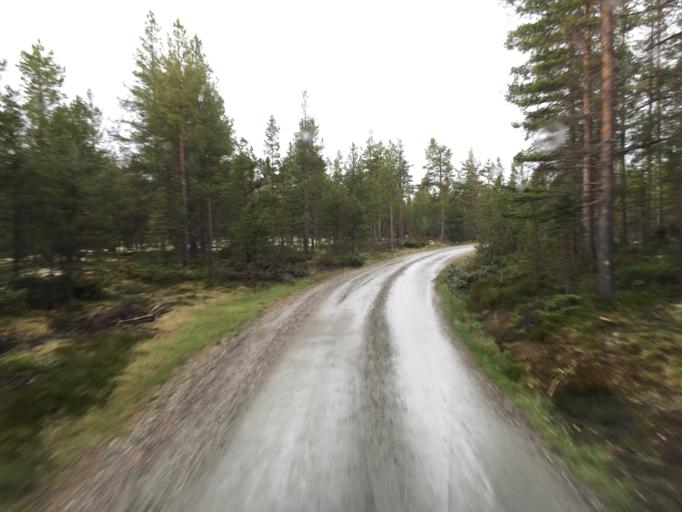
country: NO
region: Hedmark
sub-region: Folldal
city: Folldal
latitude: 62.0711
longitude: 9.9410
